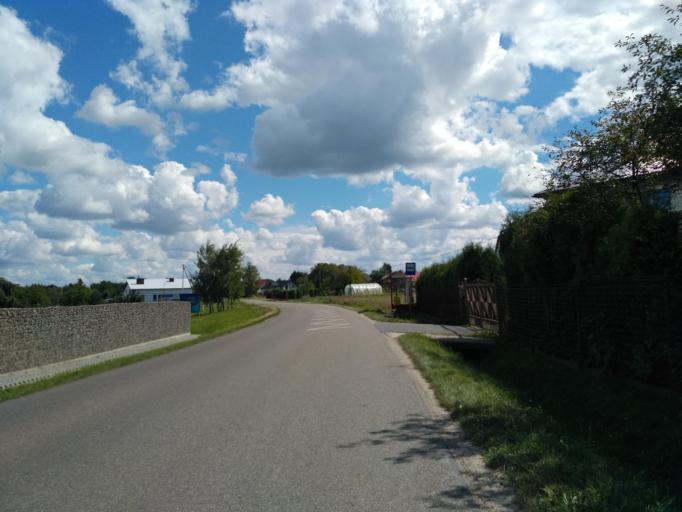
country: PL
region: Subcarpathian Voivodeship
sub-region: Powiat jasielski
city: Trzcinica
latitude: 49.7535
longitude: 21.4177
